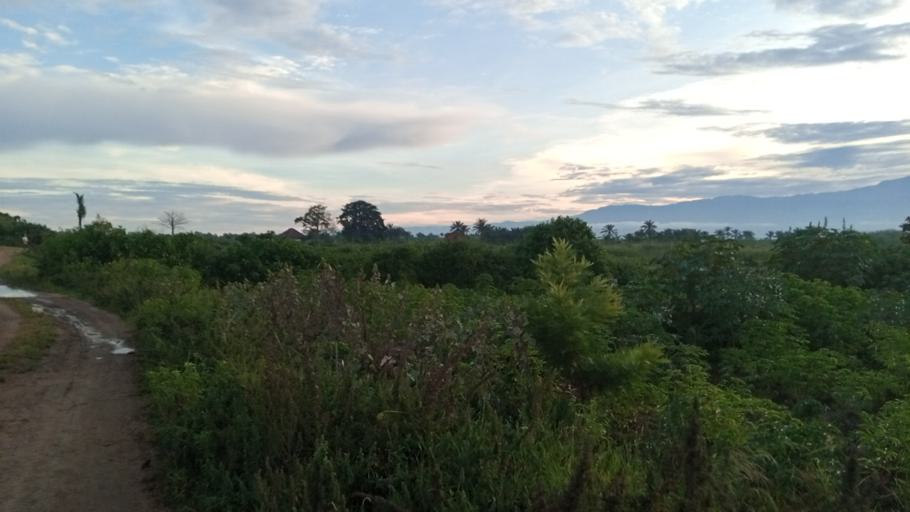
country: BI
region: Bujumbura Mairie
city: Bujumbura
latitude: -3.4697
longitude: 29.3417
